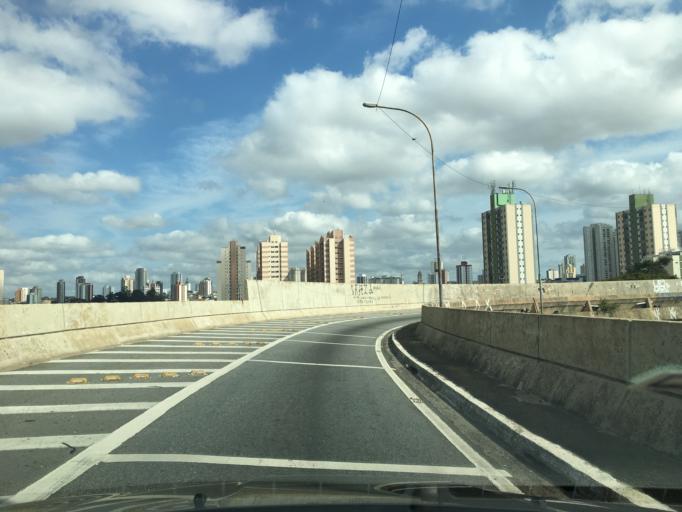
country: BR
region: Sao Paulo
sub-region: Guarulhos
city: Guarulhos
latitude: -23.5361
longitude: -46.5470
